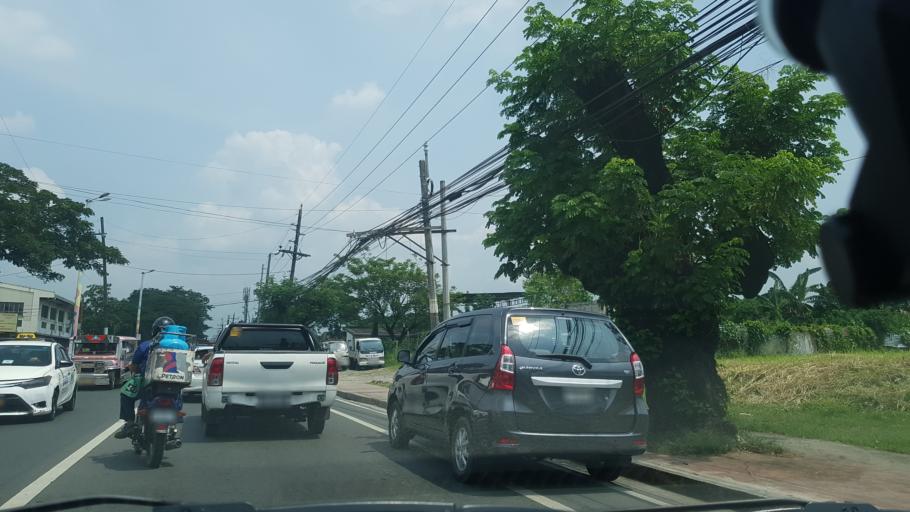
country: PH
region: Calabarzon
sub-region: Province of Rizal
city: San Mateo
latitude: 14.6653
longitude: 121.1070
